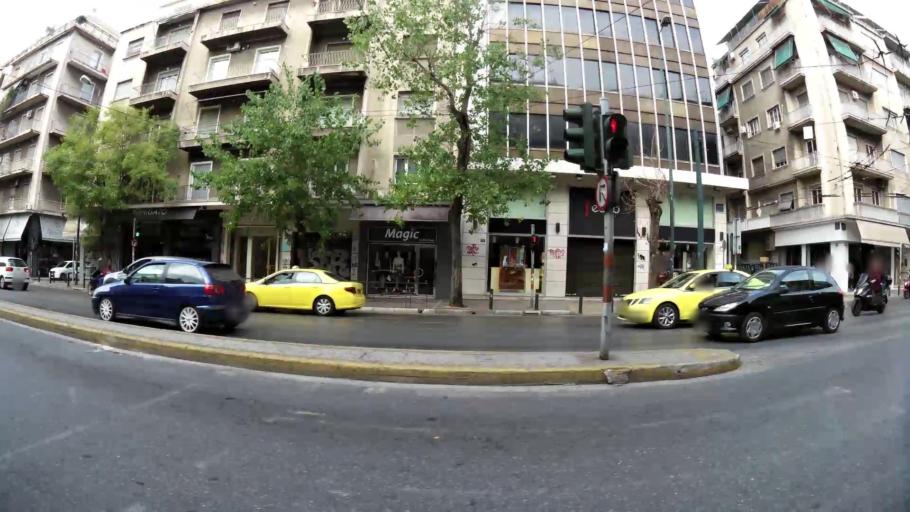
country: GR
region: Attica
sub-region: Nomarchia Athinas
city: Kipseli
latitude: 37.9964
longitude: 23.7325
